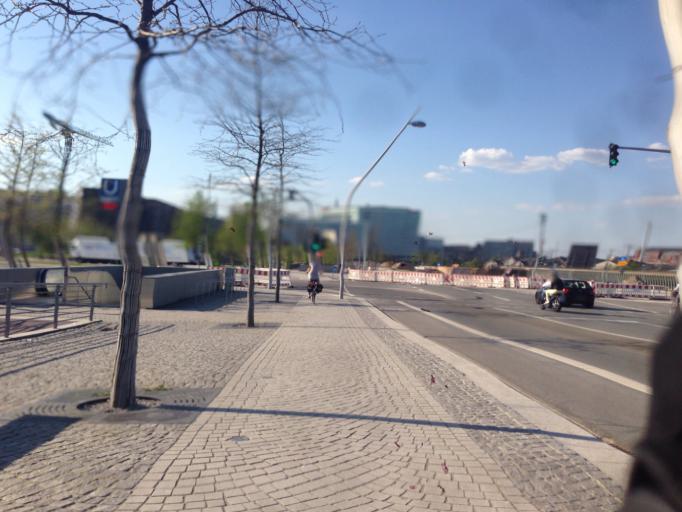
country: DE
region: Hamburg
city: Altstadt
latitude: 53.5402
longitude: 10.0072
